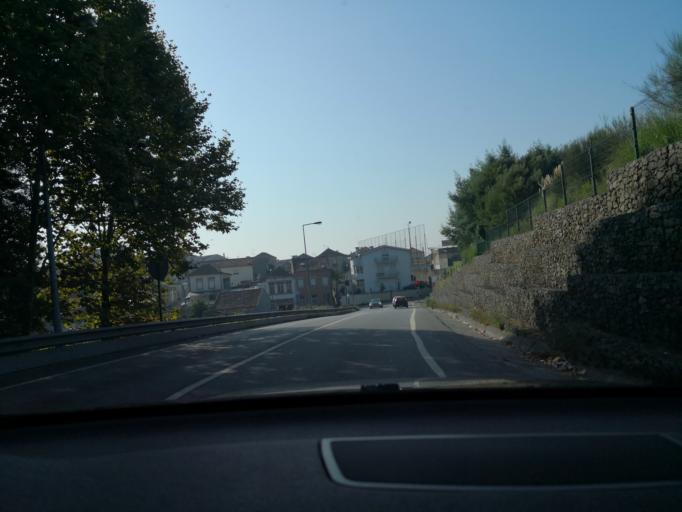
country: PT
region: Porto
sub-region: Gondomar
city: Valbom
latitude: 41.1523
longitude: -8.5826
